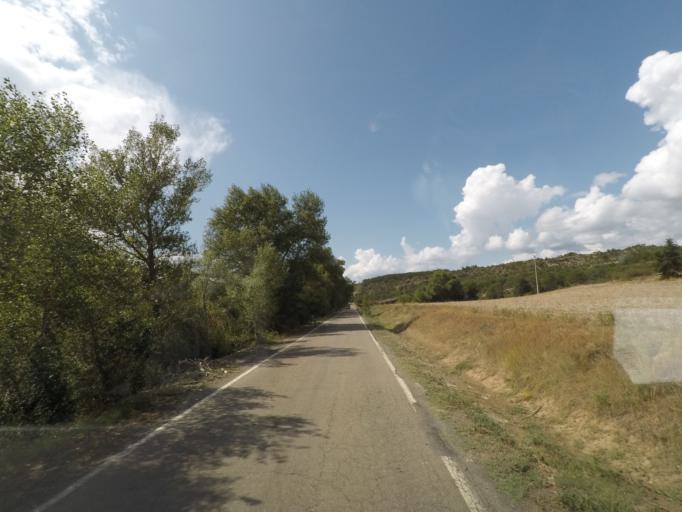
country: ES
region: Aragon
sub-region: Provincia de Huesca
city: Arguis
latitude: 42.4023
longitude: -0.3688
